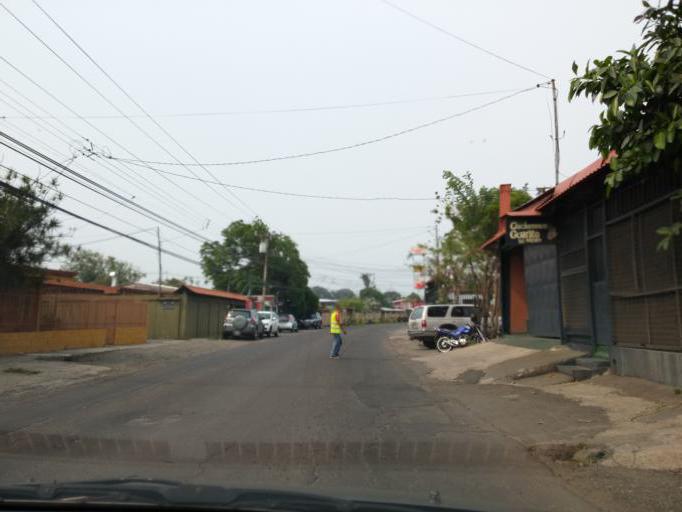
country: CR
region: Alajuela
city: Alajuela
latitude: 9.9947
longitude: -84.2295
